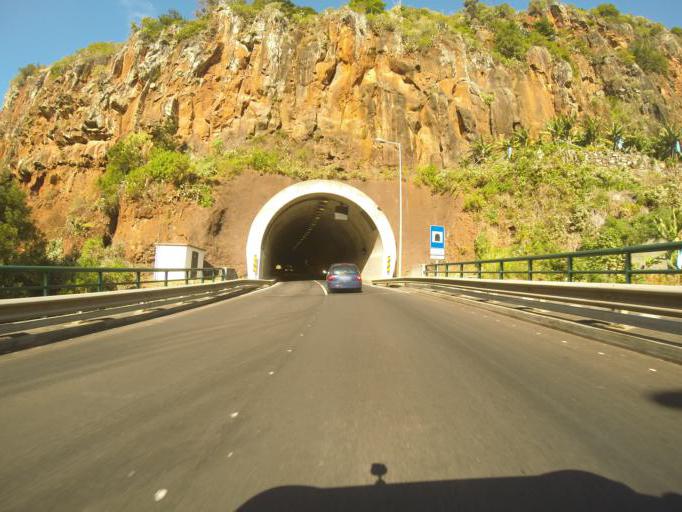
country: PT
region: Madeira
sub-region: Calheta
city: Estreito da Calheta
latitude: 32.7312
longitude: -17.1854
